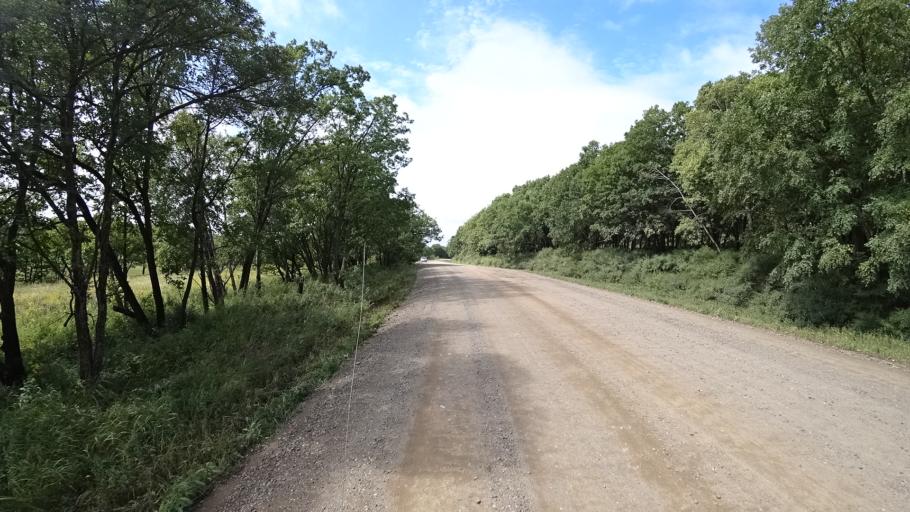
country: RU
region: Primorskiy
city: Lyalichi
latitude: 44.1477
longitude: 132.3976
